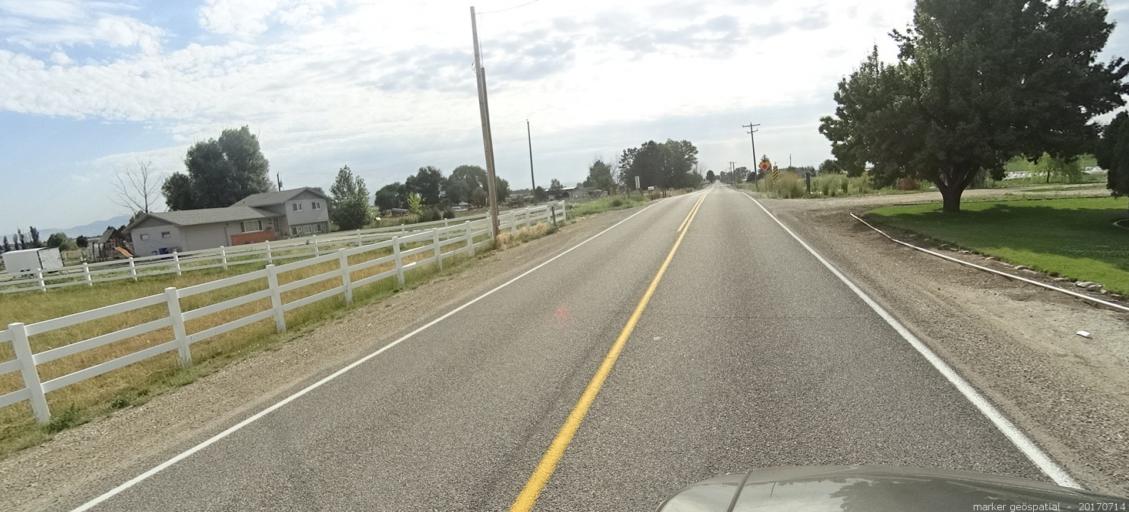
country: US
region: Idaho
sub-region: Ada County
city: Kuna
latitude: 43.4736
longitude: -116.3578
